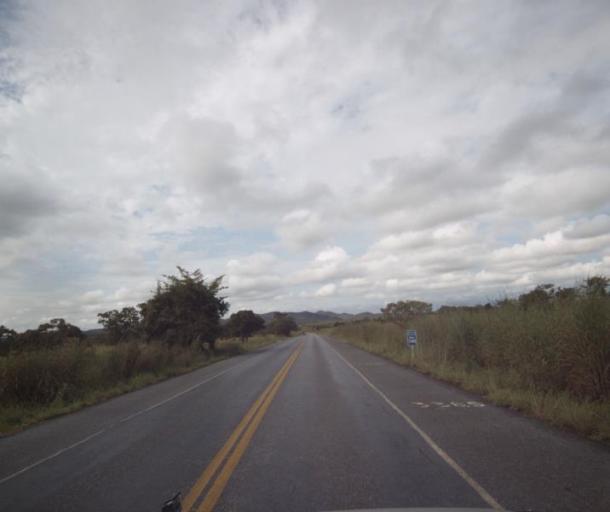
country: BR
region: Goias
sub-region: Pirenopolis
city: Pirenopolis
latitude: -15.5508
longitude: -48.6229
